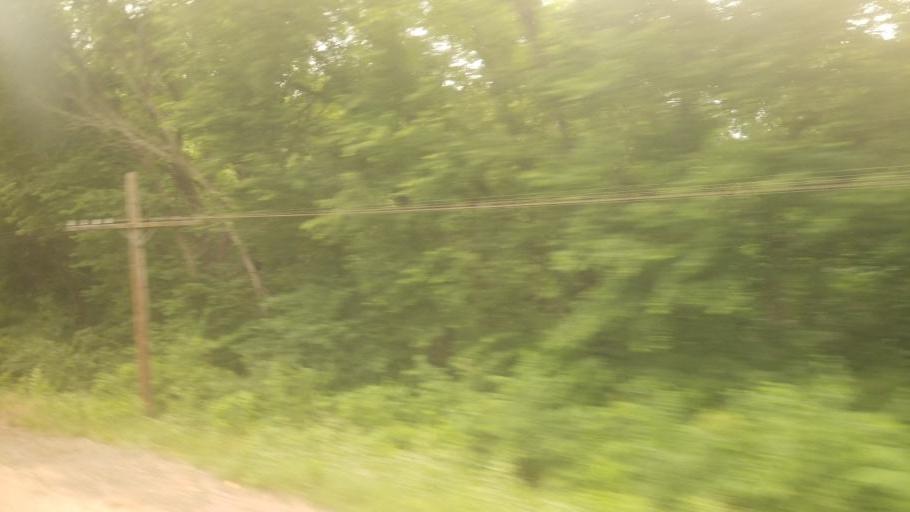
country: US
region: Kansas
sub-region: Osage County
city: Carbondale
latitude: 38.8866
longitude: -95.6963
